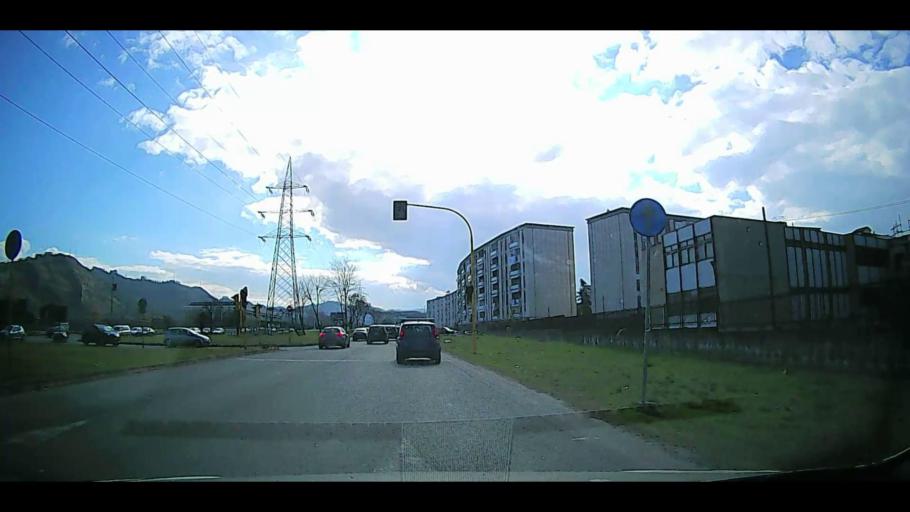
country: IT
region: Calabria
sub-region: Provincia di Cosenza
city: Cosenza
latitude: 39.3181
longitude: 16.2573
